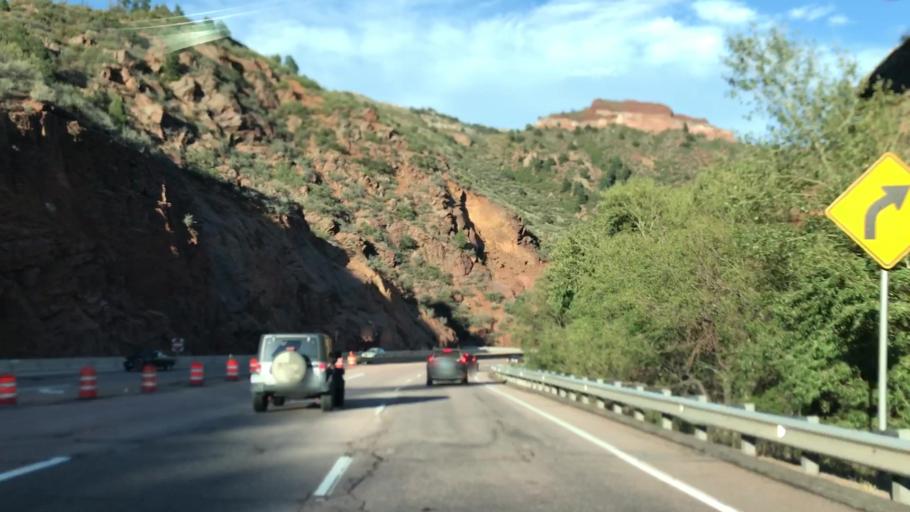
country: US
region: Colorado
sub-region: El Paso County
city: Manitou Springs
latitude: 38.8762
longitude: -104.9344
